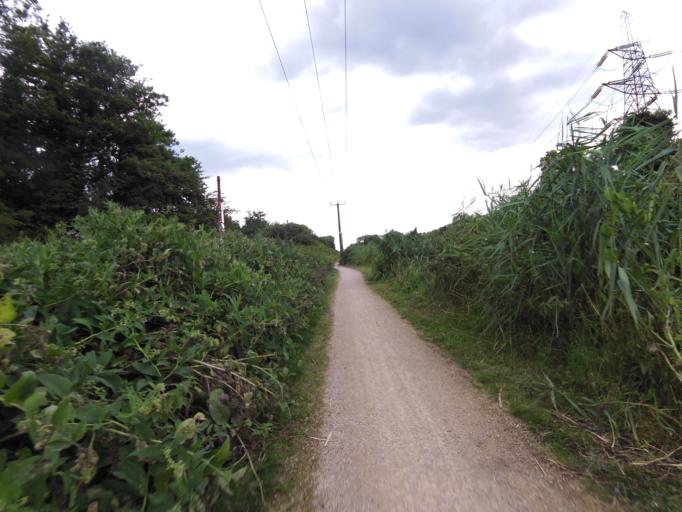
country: GB
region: England
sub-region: Hertfordshire
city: Cheshunt
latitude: 51.7193
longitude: -0.0148
